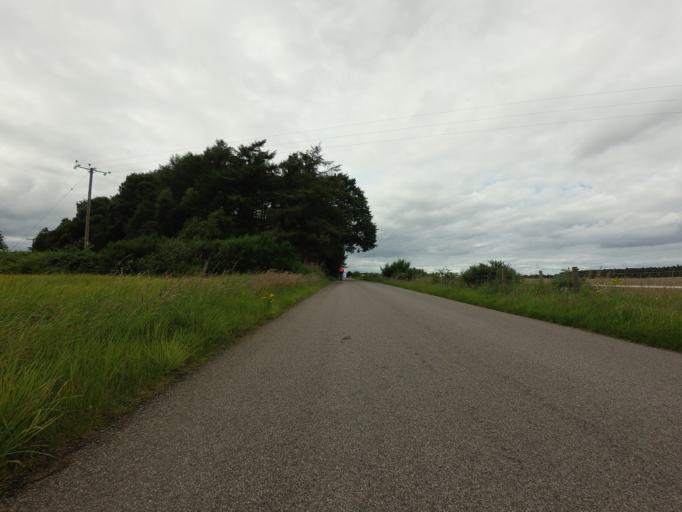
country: GB
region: Scotland
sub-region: Moray
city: Forres
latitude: 57.6020
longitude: -3.7244
